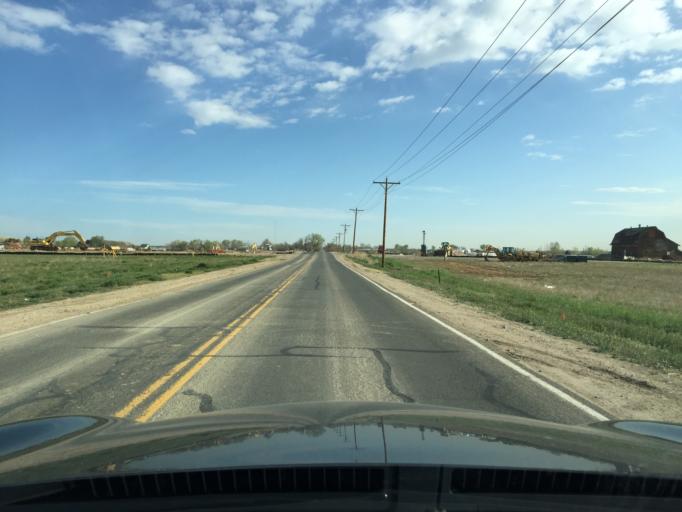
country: US
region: Colorado
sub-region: Boulder County
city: Erie
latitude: 40.0028
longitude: -104.9991
